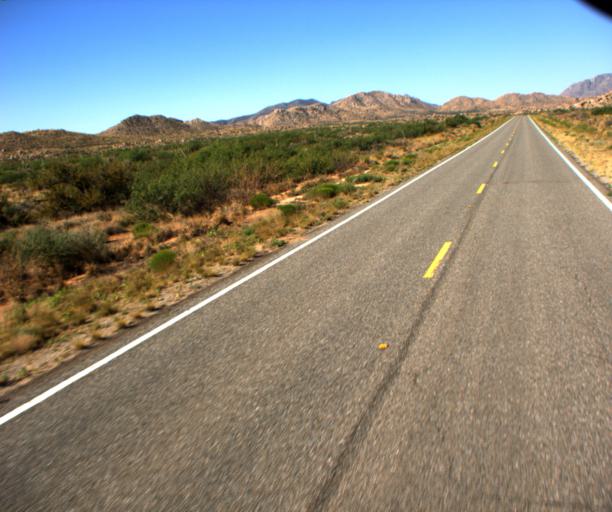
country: US
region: Arizona
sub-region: Graham County
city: Swift Trail Junction
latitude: 32.5812
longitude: -109.7070
